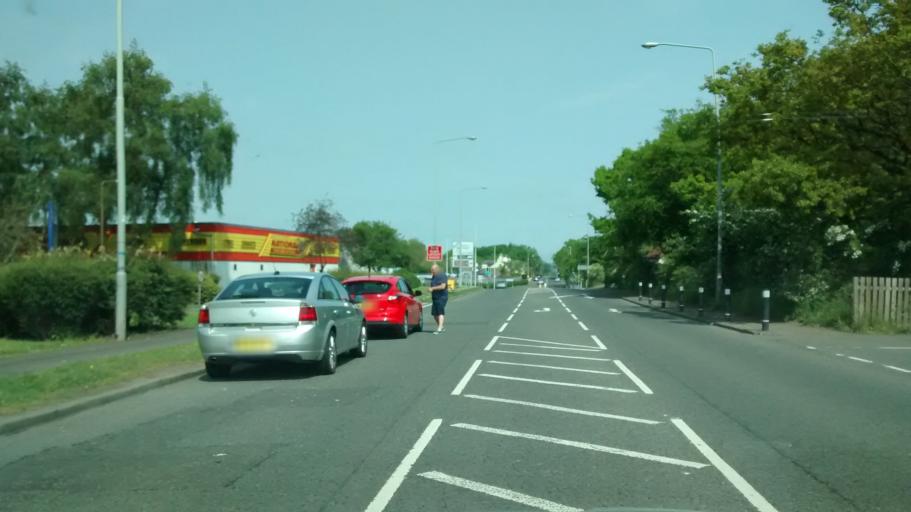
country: GB
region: Scotland
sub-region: West Lothian
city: Mid Calder
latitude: 55.9097
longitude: -3.4959
